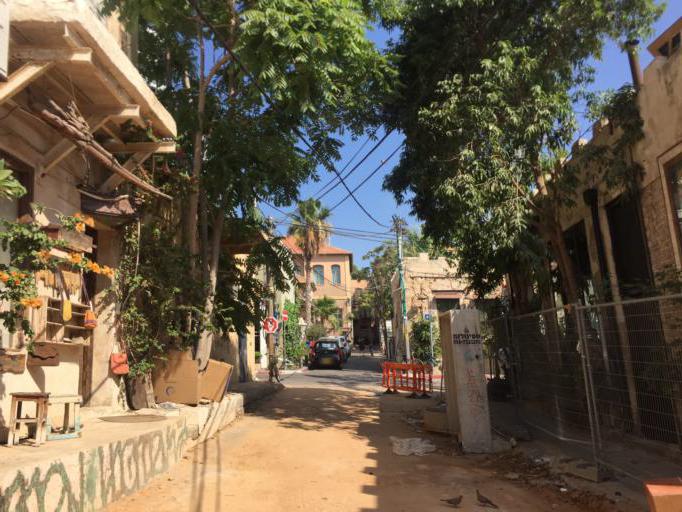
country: IL
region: Tel Aviv
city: Yafo
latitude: 32.0634
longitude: 34.7681
